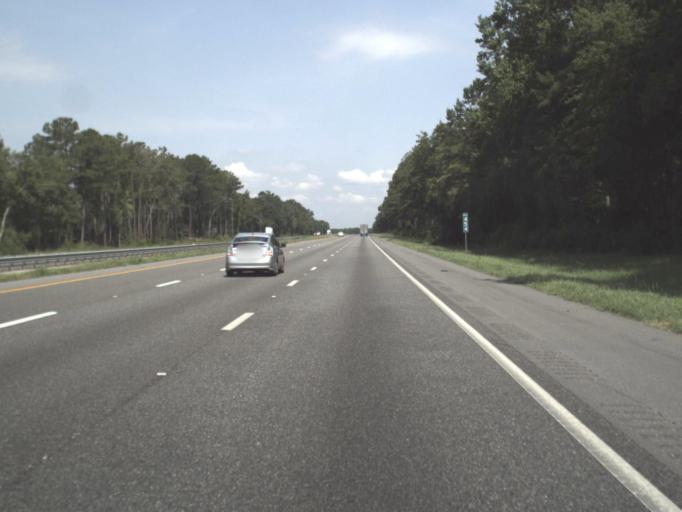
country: US
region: Florida
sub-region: Hamilton County
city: Jasper
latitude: 30.4704
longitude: -82.9685
